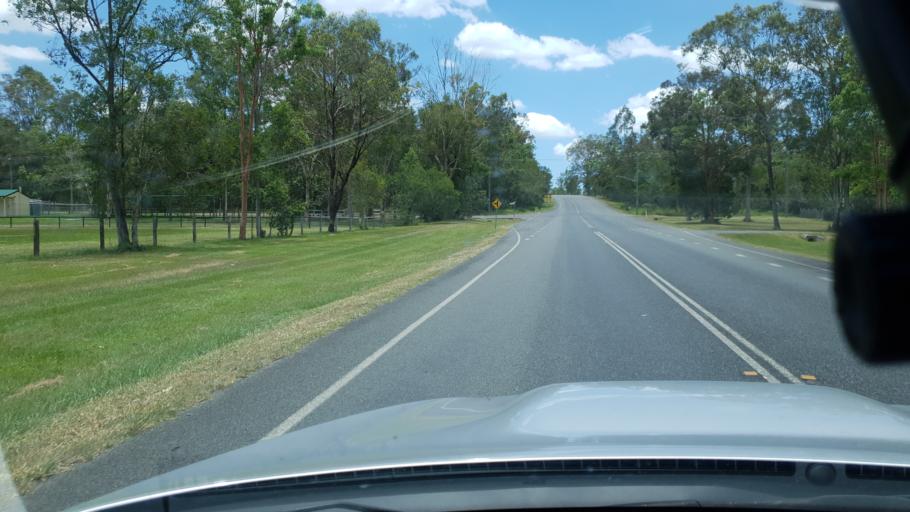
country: AU
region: Queensland
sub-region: Logan
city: North Maclean
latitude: -27.7683
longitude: 152.9836
